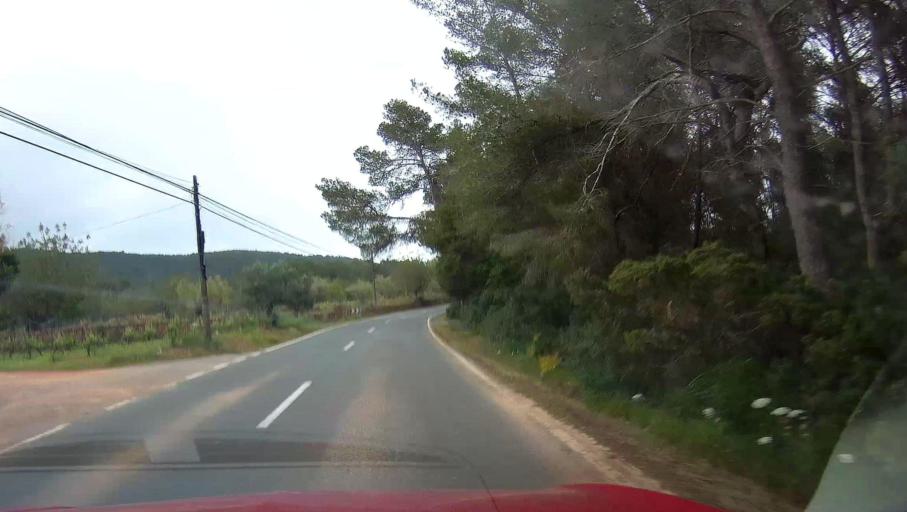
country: ES
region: Balearic Islands
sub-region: Illes Balears
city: Sant Joan de Labritja
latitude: 39.0673
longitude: 1.4878
